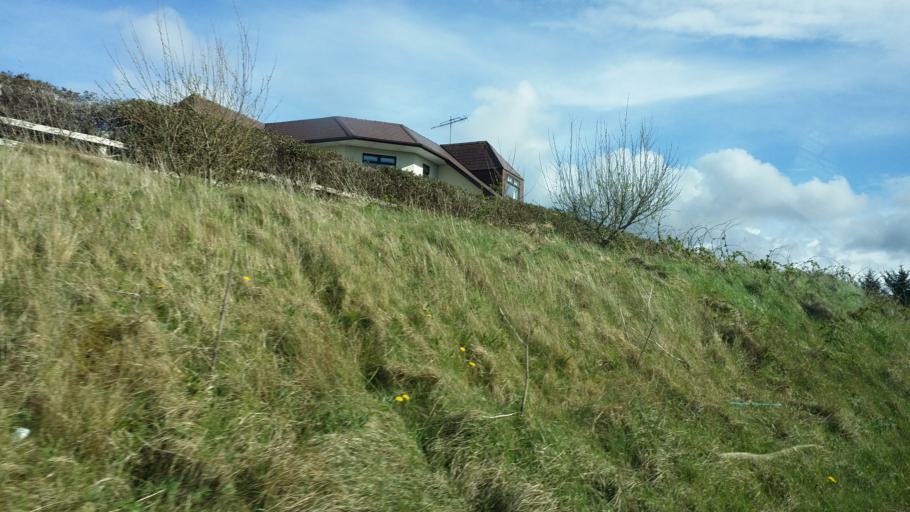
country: IE
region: Ulster
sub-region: County Donegal
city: Bundoran
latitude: 54.4701
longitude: -8.2767
